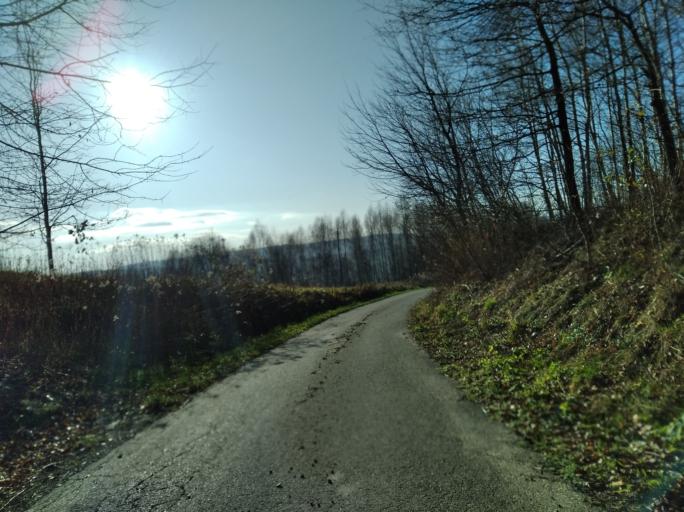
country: PL
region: Subcarpathian Voivodeship
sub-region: Powiat strzyzowski
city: Strzyzow
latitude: 49.8789
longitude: 21.8299
